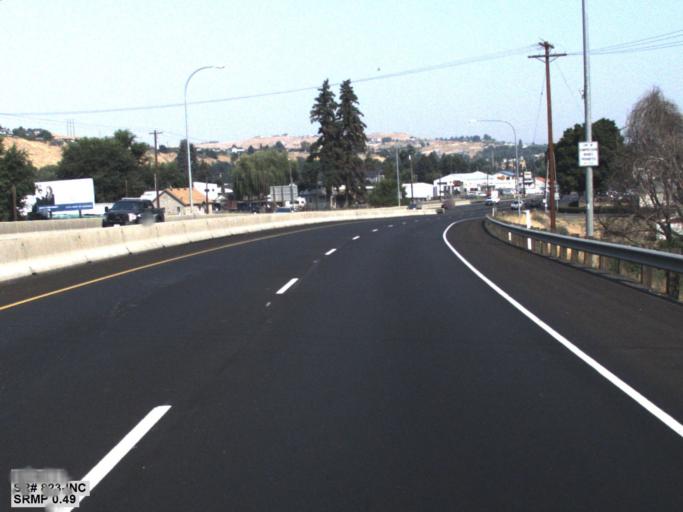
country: US
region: Washington
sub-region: Yakima County
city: Selah
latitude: 46.6402
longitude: -120.5295
